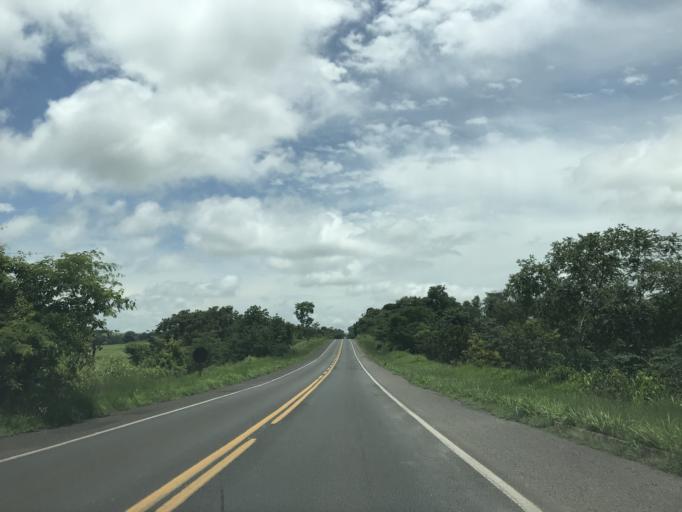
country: BR
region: Minas Gerais
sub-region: Prata
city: Prata
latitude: -19.6284
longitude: -48.9260
